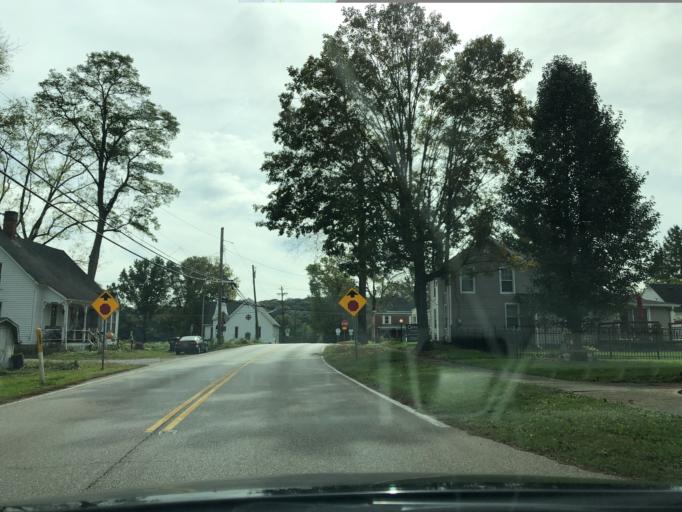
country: US
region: Ohio
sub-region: Hamilton County
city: The Village of Indian Hill
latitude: 39.2138
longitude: -84.2985
